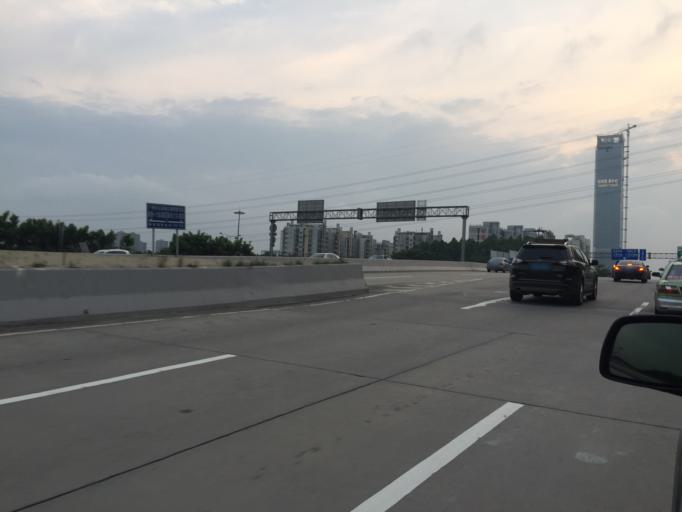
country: CN
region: Guangdong
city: Wushan
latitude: 23.1014
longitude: 113.3468
